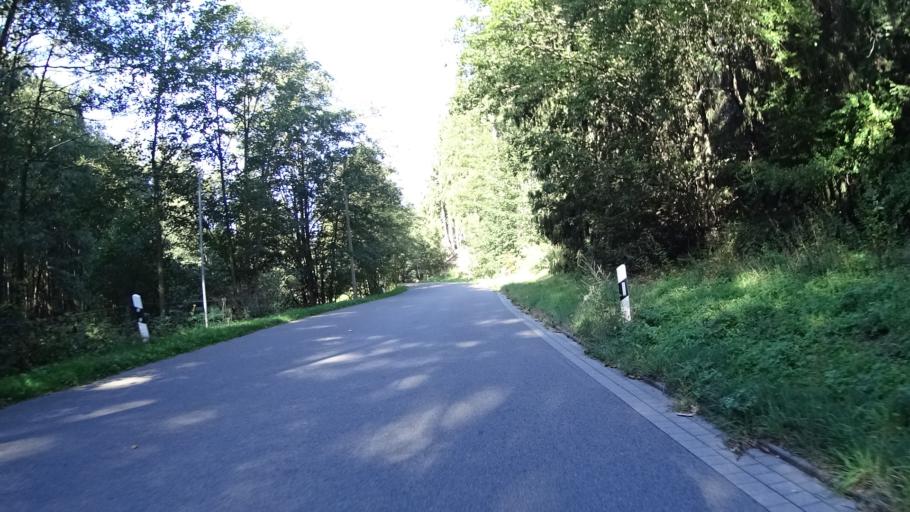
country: DE
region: Thuringia
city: Mohrenbach
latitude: 50.6448
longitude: 10.9807
